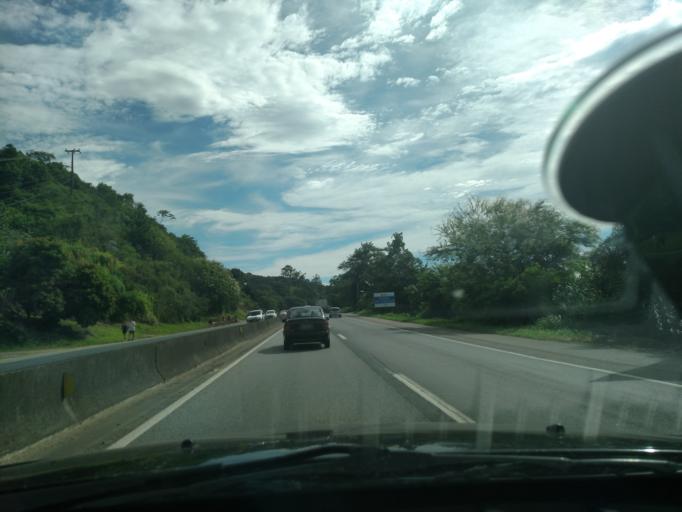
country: BR
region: Santa Catarina
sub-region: Biguacu
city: Biguacu
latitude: -27.4833
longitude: -48.6469
